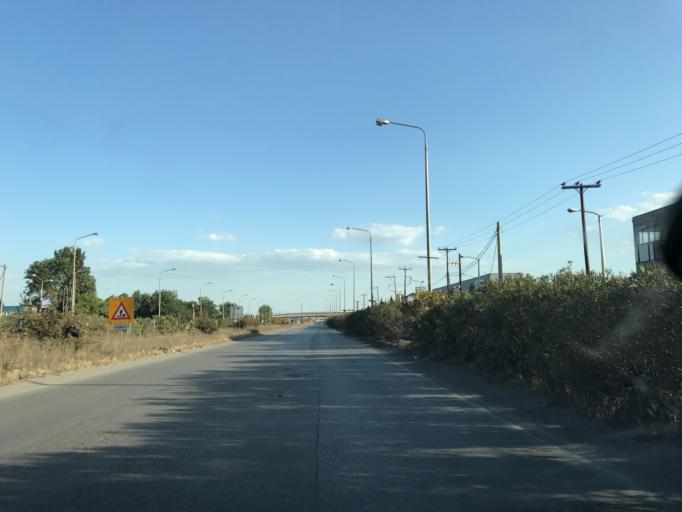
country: GR
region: Central Macedonia
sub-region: Nomos Thessalonikis
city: Menemeni
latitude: 40.6622
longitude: 22.8816
